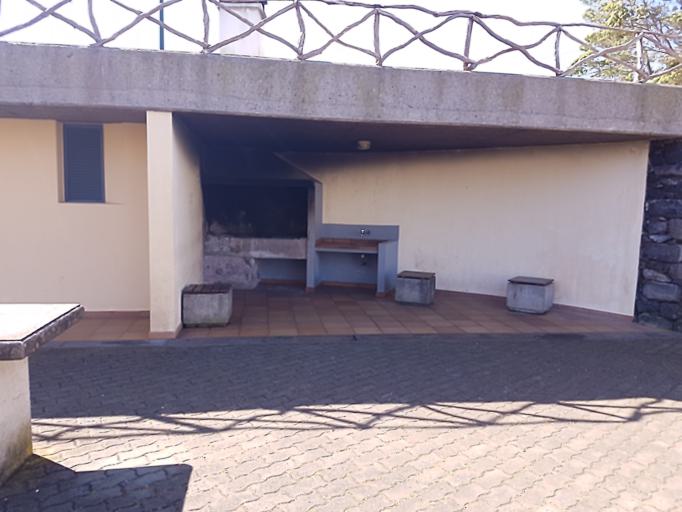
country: PT
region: Madeira
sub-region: Porto Moniz
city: Porto Moniz
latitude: 32.8516
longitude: -17.1664
